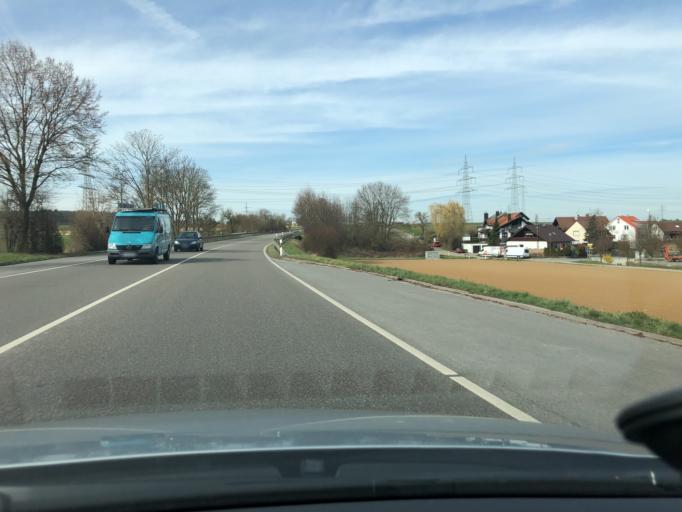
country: DE
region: Baden-Wuerttemberg
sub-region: Regierungsbezirk Stuttgart
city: Hemmingen
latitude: 48.8908
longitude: 9.0288
